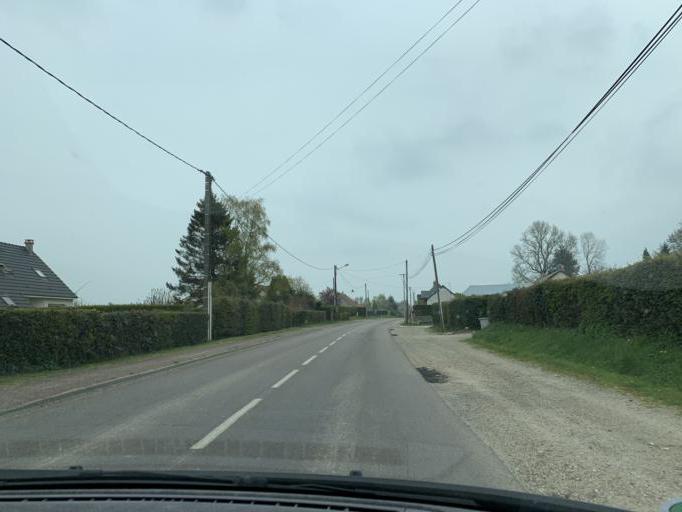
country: FR
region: Haute-Normandie
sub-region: Departement de la Seine-Maritime
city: Londinieres
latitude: 49.8409
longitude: 1.4792
